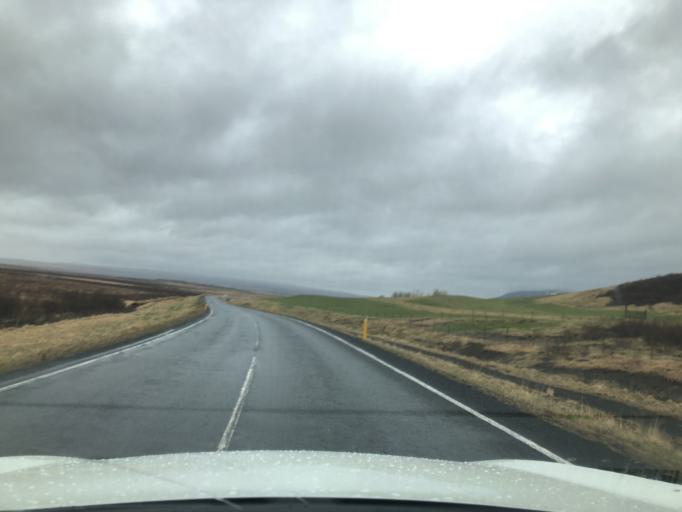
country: IS
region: South
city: Selfoss
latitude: 64.2256
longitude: -20.6044
